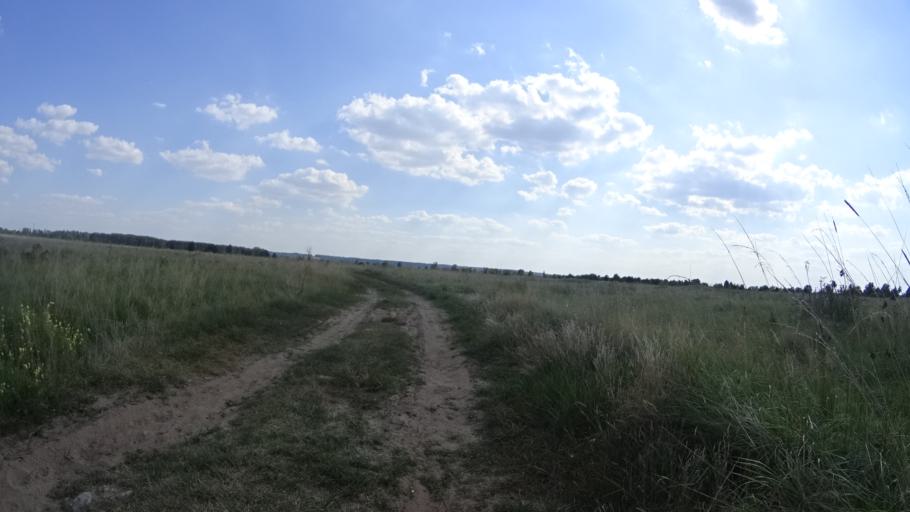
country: PL
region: Masovian Voivodeship
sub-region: Powiat bialobrzeski
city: Wysmierzyce
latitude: 51.6512
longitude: 20.8275
